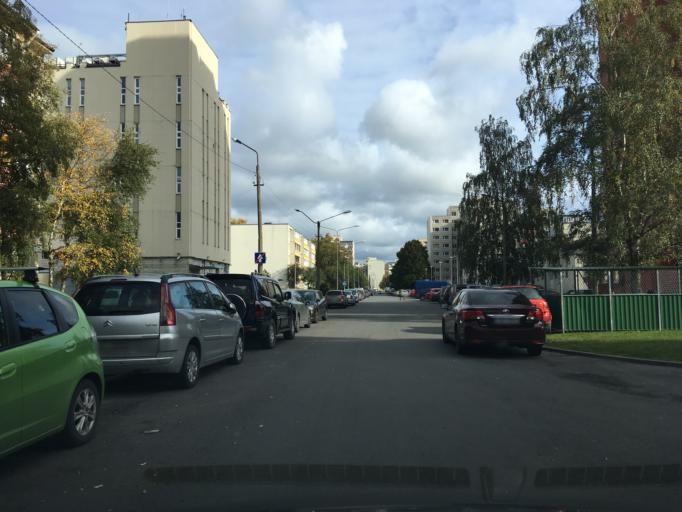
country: EE
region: Harju
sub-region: Tallinna linn
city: Kose
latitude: 59.4406
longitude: 24.8293
